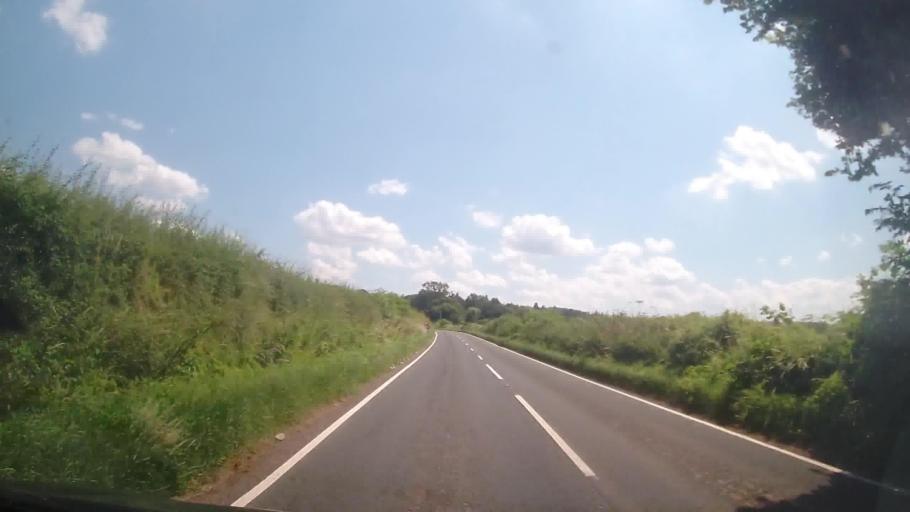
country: GB
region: England
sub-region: Herefordshire
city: Brockhampton
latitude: 51.9786
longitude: -2.5604
